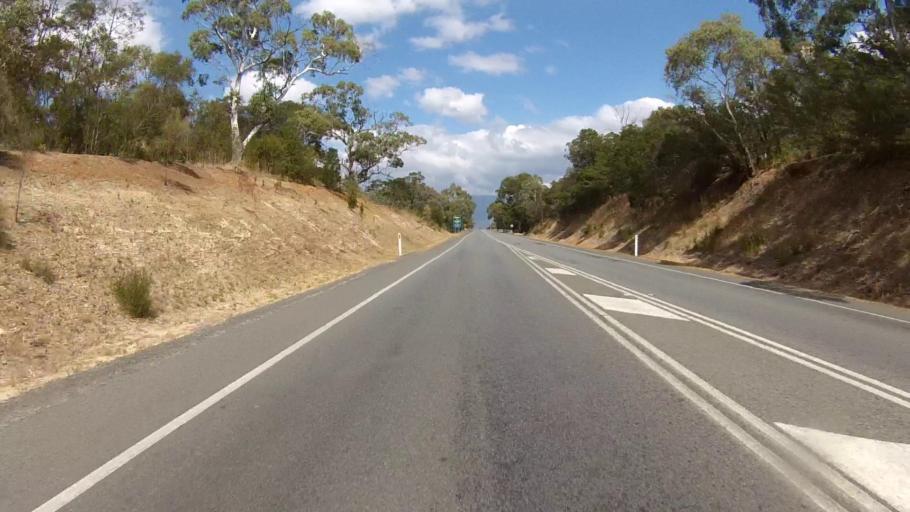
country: AU
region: Tasmania
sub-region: Brighton
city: Old Beach
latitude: -42.7672
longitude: 147.2700
